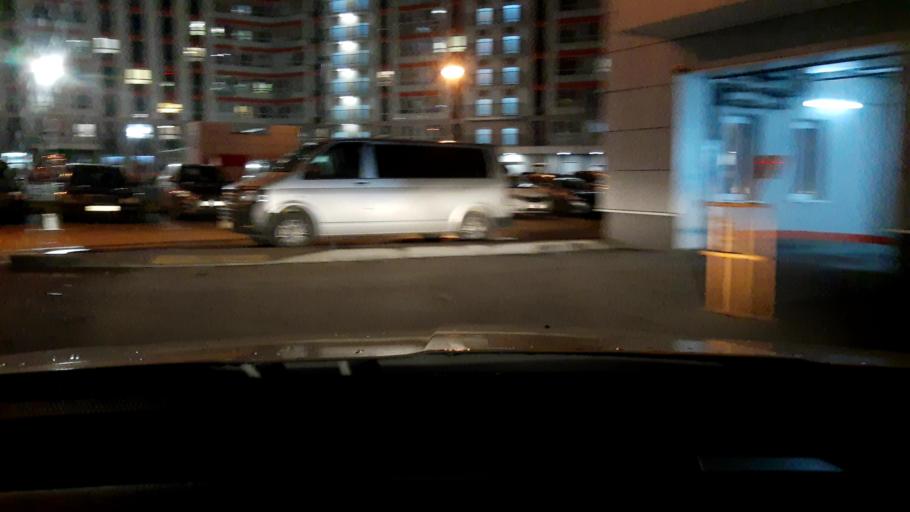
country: RU
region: Moscow
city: Severnyy
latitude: 55.9253
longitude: 37.5494
